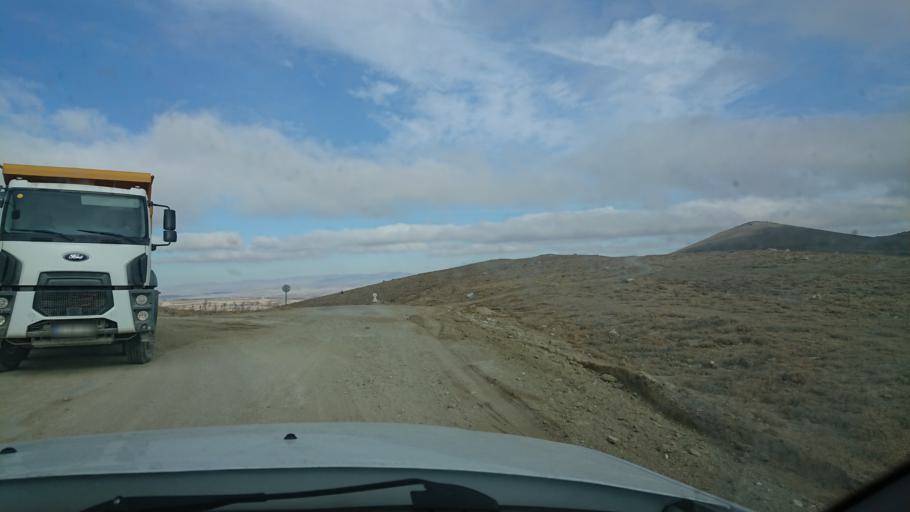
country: TR
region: Aksaray
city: Ortakoy
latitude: 38.7823
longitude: 34.0041
